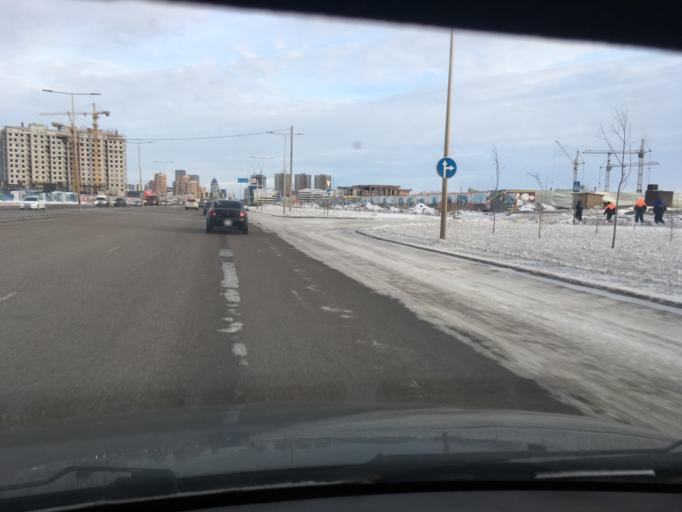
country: KZ
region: Astana Qalasy
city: Astana
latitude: 51.1285
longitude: 71.3923
